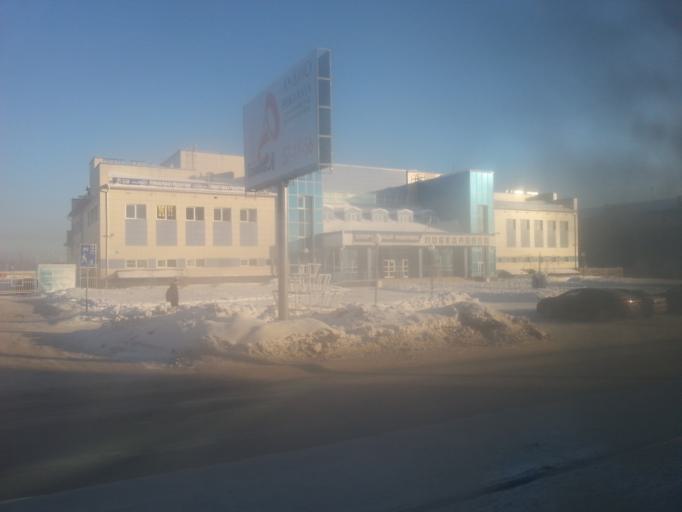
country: RU
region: Altai Krai
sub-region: Gorod Barnaulskiy
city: Barnaul
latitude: 53.3566
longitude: 83.7117
